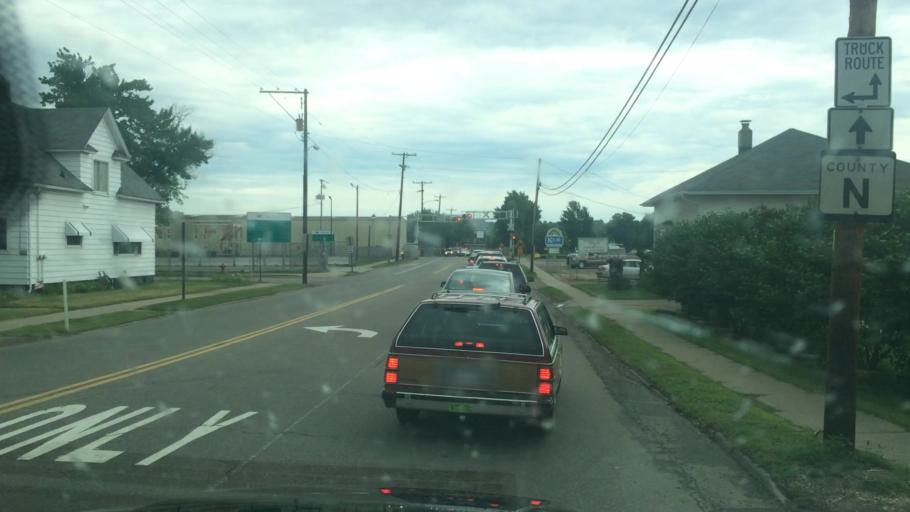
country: US
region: Wisconsin
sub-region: Marathon County
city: Wausau
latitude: 44.9484
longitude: -89.6389
